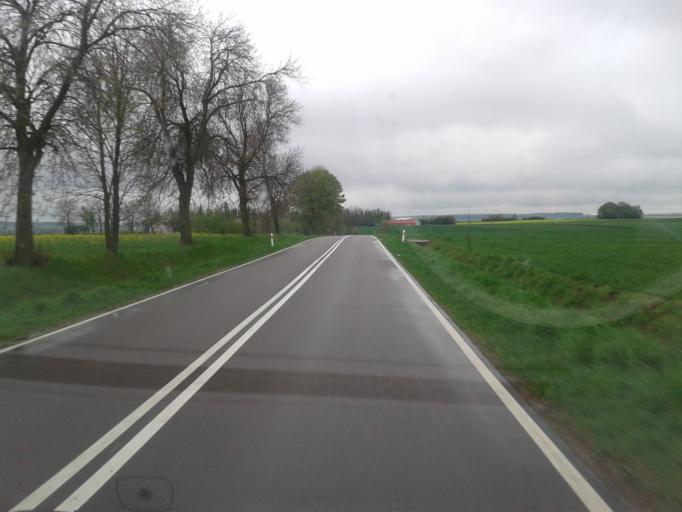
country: PL
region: Lublin Voivodeship
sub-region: Powiat tomaszowski
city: Telatyn
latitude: 50.5450
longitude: 23.9264
